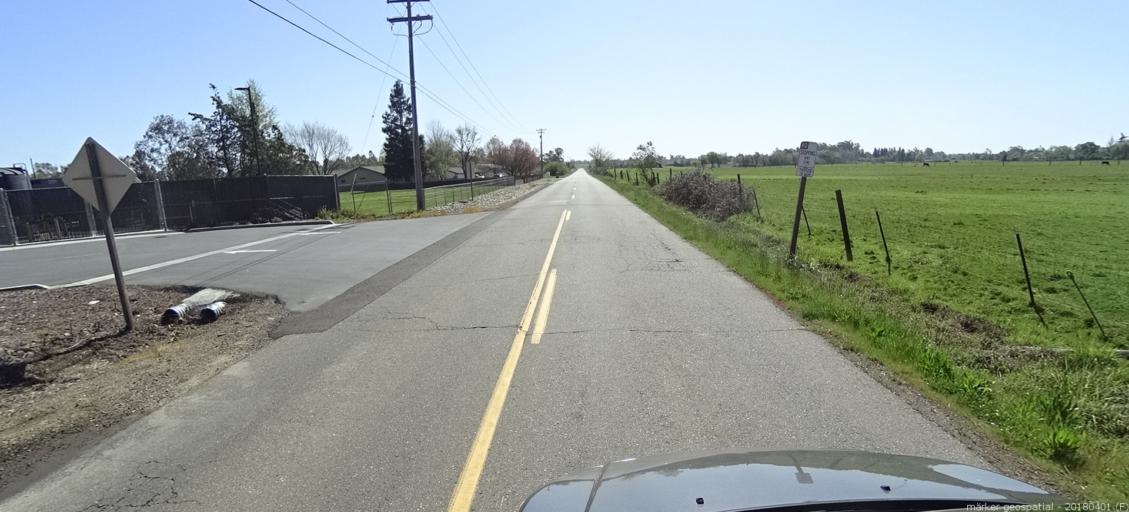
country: US
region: California
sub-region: Sacramento County
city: Wilton
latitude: 38.4033
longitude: -121.2506
